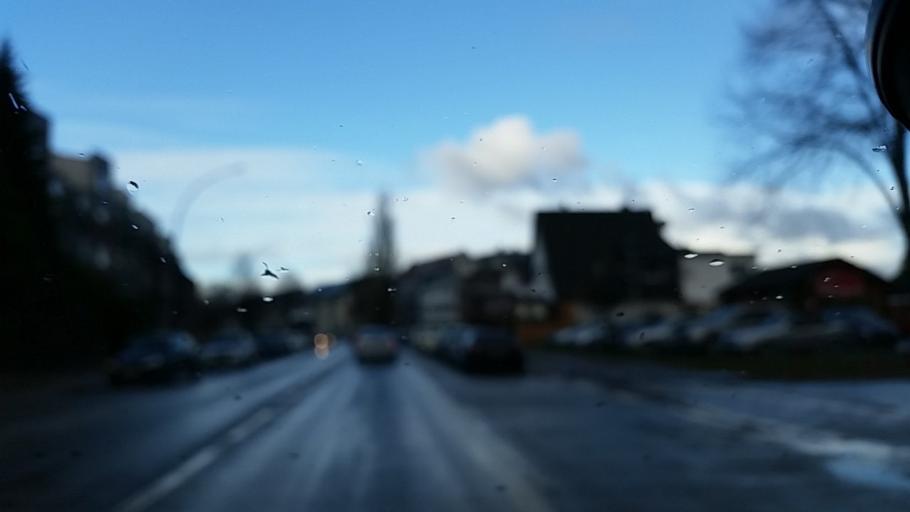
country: DE
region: Hamburg
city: Eidelstedt
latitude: 53.5953
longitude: 9.8683
